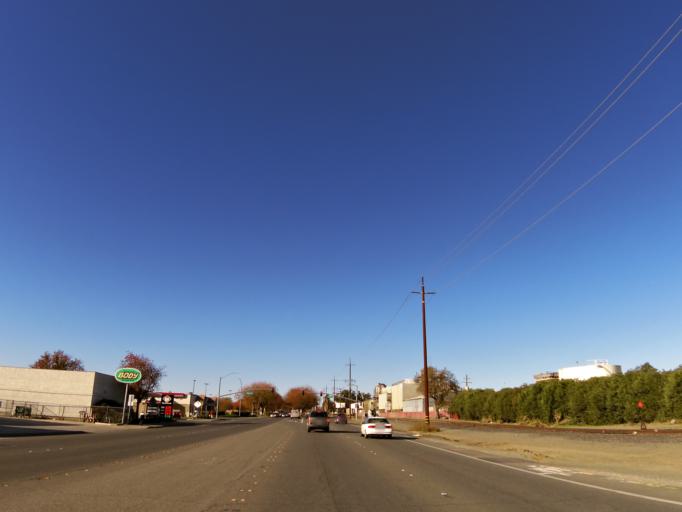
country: US
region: California
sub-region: Yolo County
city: Woodland
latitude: 38.6773
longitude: -121.7546
